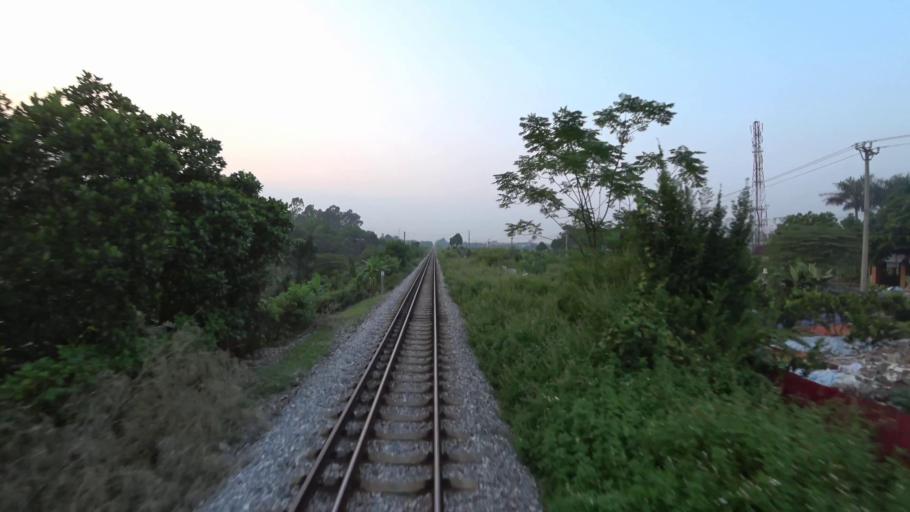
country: VN
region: Ha Noi
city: Dong Anh
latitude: 21.1318
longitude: 105.8746
